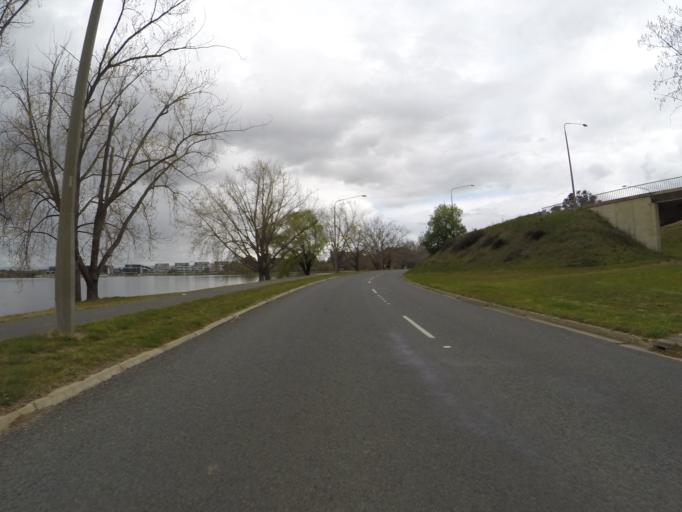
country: AU
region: Australian Capital Territory
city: Forrest
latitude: -35.3040
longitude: 149.1405
